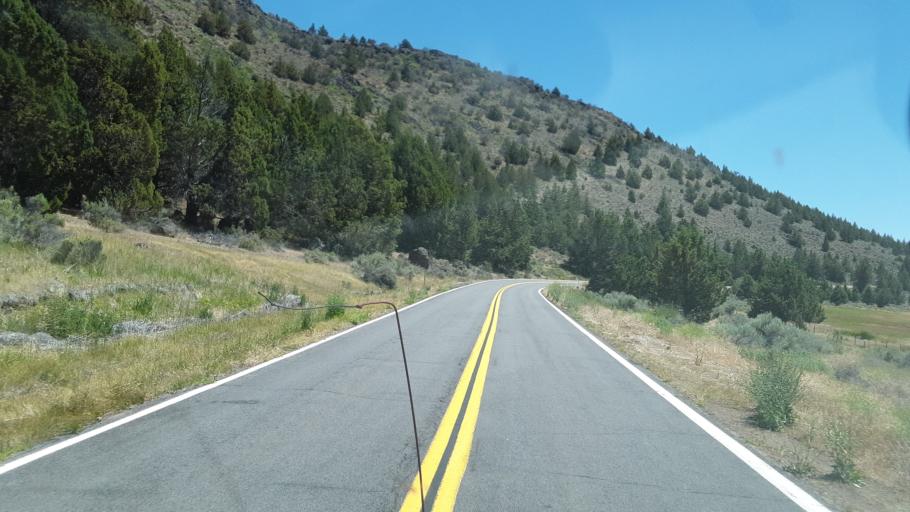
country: US
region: California
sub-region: Lassen County
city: Susanville
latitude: 40.6606
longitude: -120.6571
